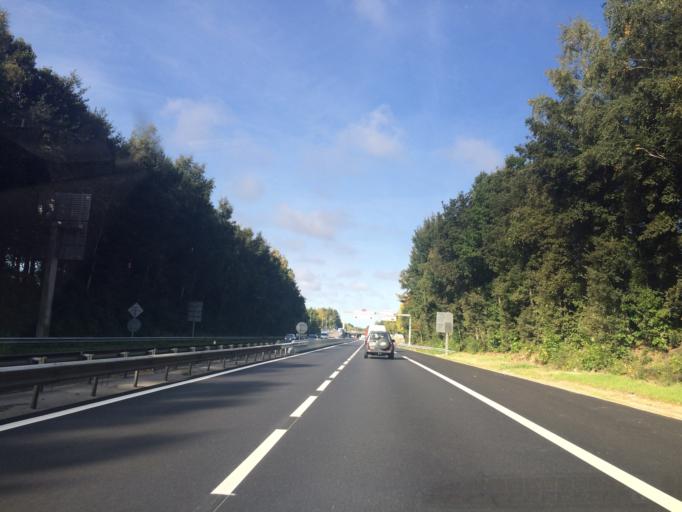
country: FR
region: Pays de la Loire
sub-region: Departement de la Loire-Atlantique
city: Sainte-Luce-sur-Loire
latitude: 47.2547
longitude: -1.5241
